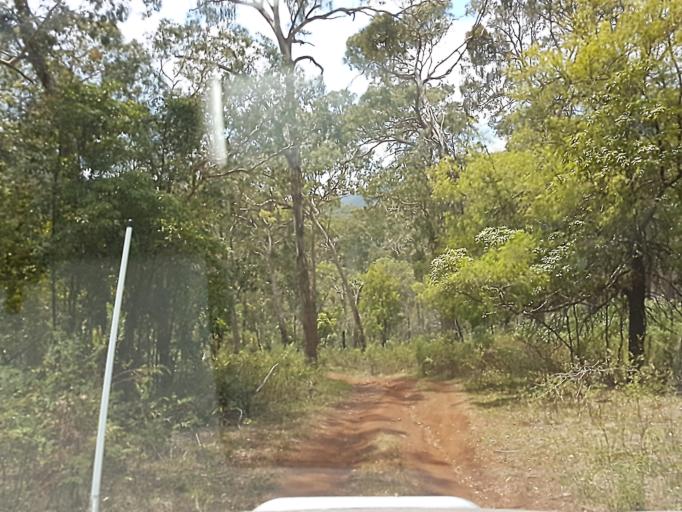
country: AU
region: Victoria
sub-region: East Gippsland
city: Lakes Entrance
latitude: -37.3567
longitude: 148.3567
